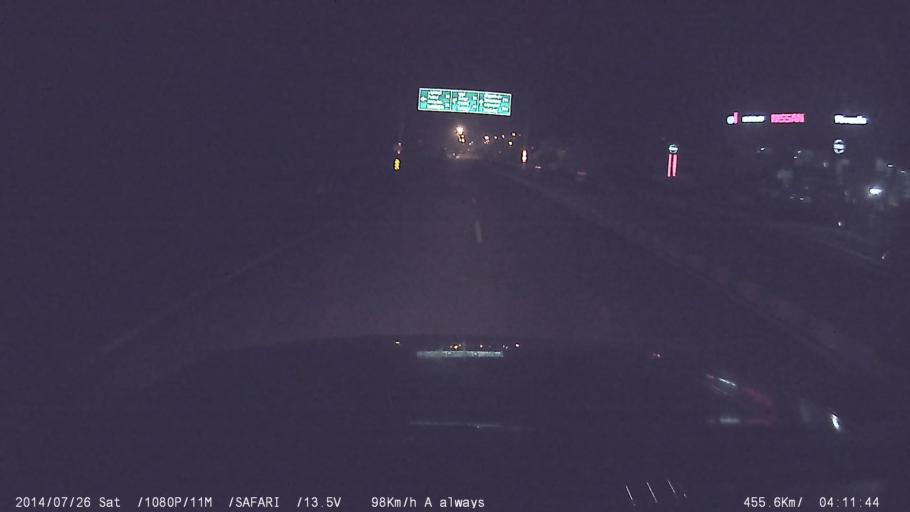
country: IN
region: Kerala
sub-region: Thrissur District
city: Trichur
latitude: 10.5022
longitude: 76.2583
